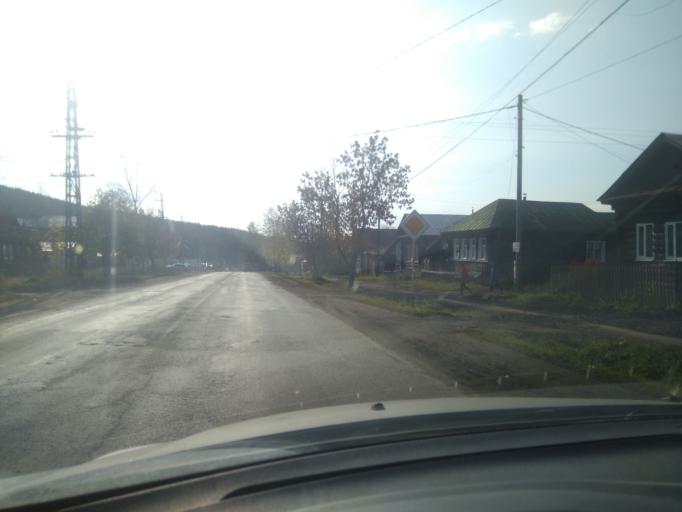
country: RU
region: Sverdlovsk
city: Nizhniye Sergi
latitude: 56.6601
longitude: 59.3006
